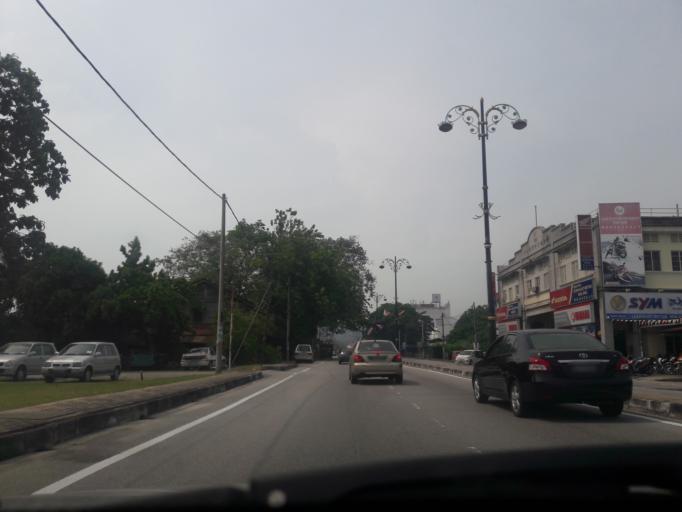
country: MY
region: Kedah
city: Kulim
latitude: 5.3752
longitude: 100.5542
